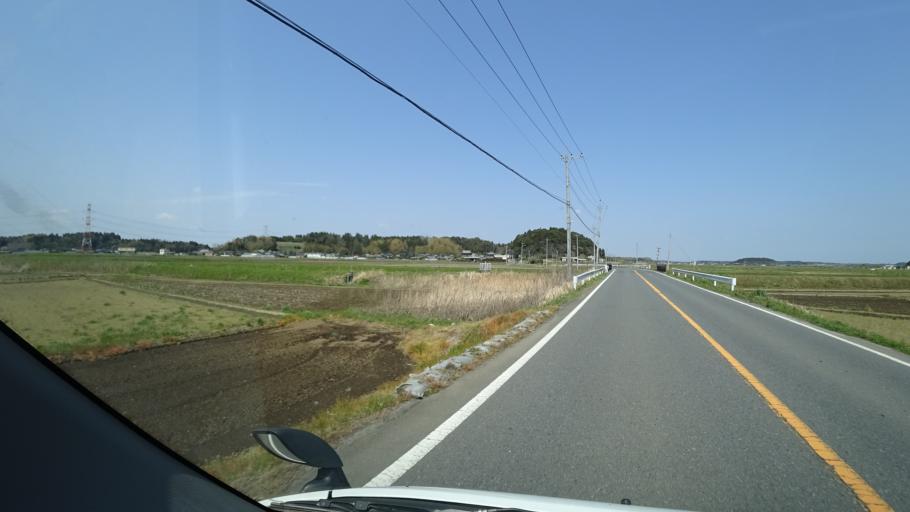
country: JP
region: Chiba
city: Yokaichiba
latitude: 35.6904
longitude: 140.4605
